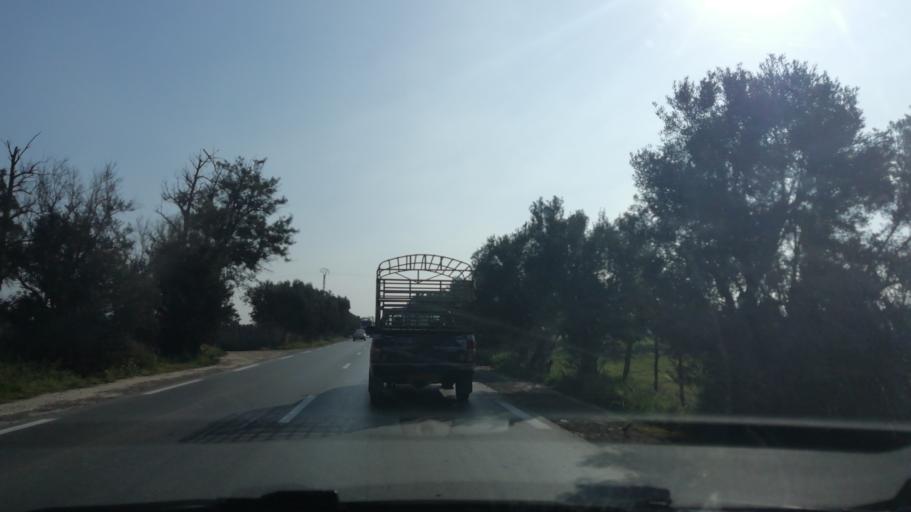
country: DZ
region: Mostaganem
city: Mostaganem
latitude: 35.7421
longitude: -0.0048
